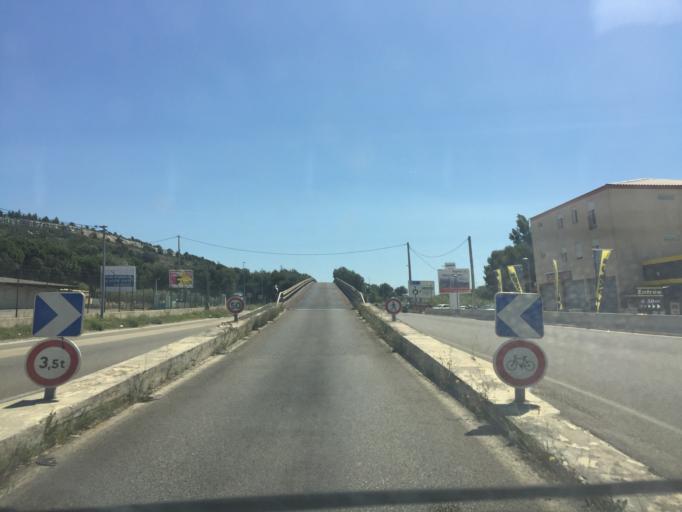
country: FR
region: Provence-Alpes-Cote d'Azur
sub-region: Departement des Bouches-du-Rhone
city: Vitrolles
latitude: 43.4609
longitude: 5.2325
